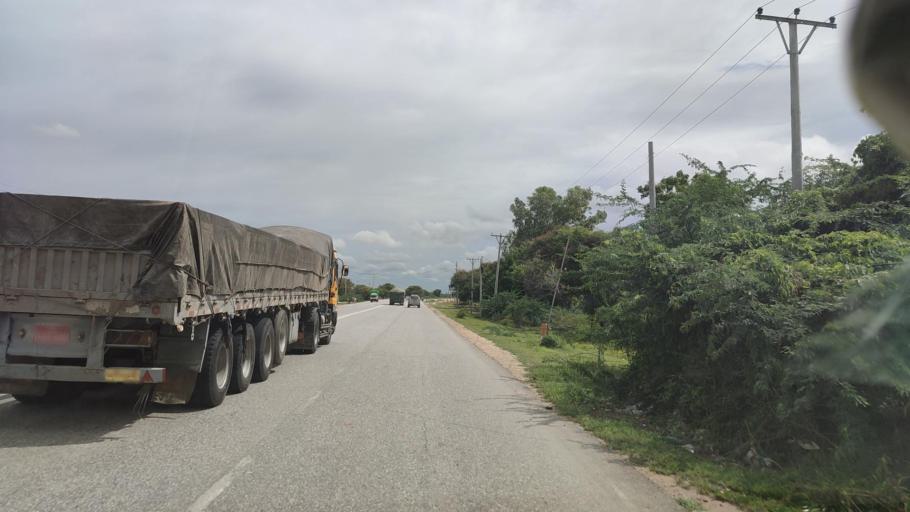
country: MM
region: Mandalay
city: Meiktila
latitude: 21.0436
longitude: 95.9961
